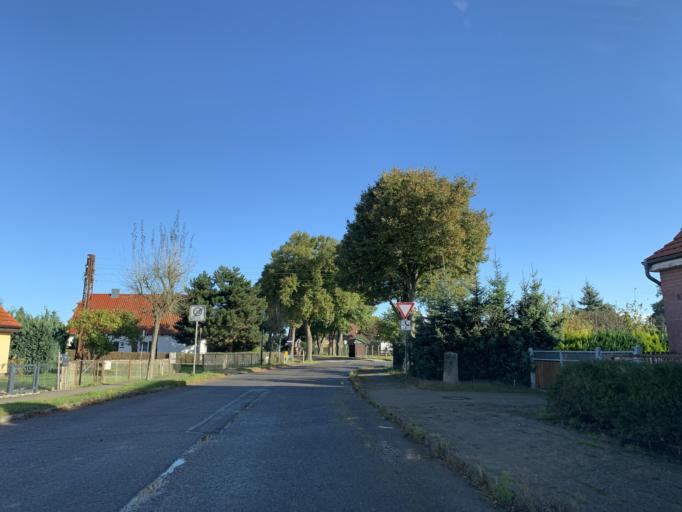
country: DE
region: Mecklenburg-Vorpommern
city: Burg Stargard
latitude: 53.4861
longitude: 13.2702
